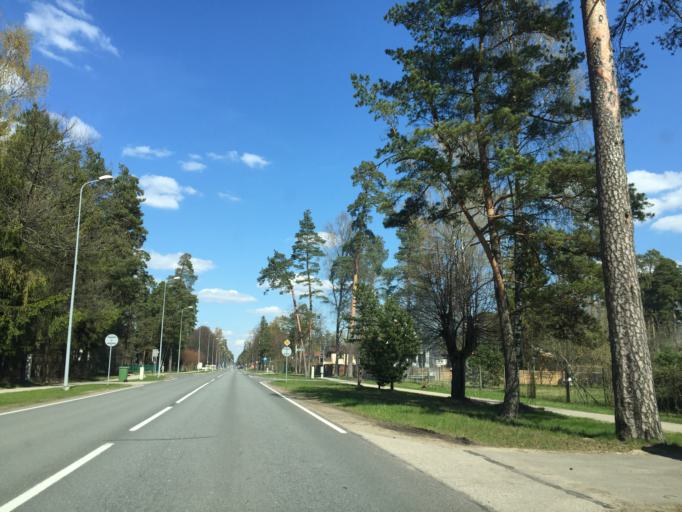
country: LV
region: Saulkrastu
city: Saulkrasti
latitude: 57.2403
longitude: 24.3990
